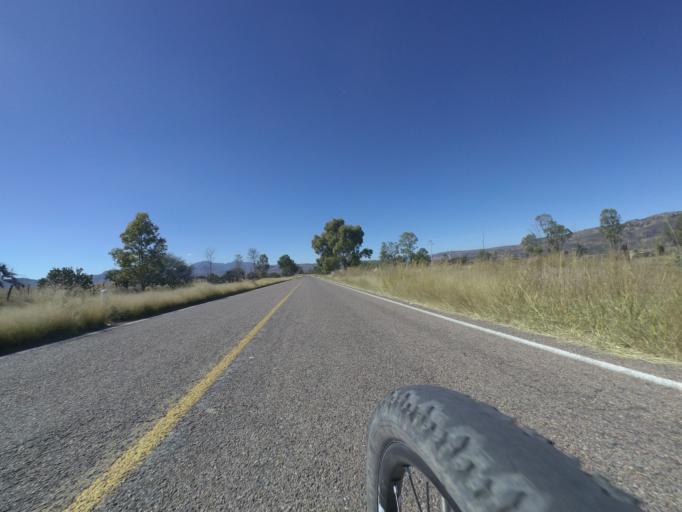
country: MX
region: Aguascalientes
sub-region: Aguascalientes
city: Los Canos
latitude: 21.8650
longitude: -102.5031
